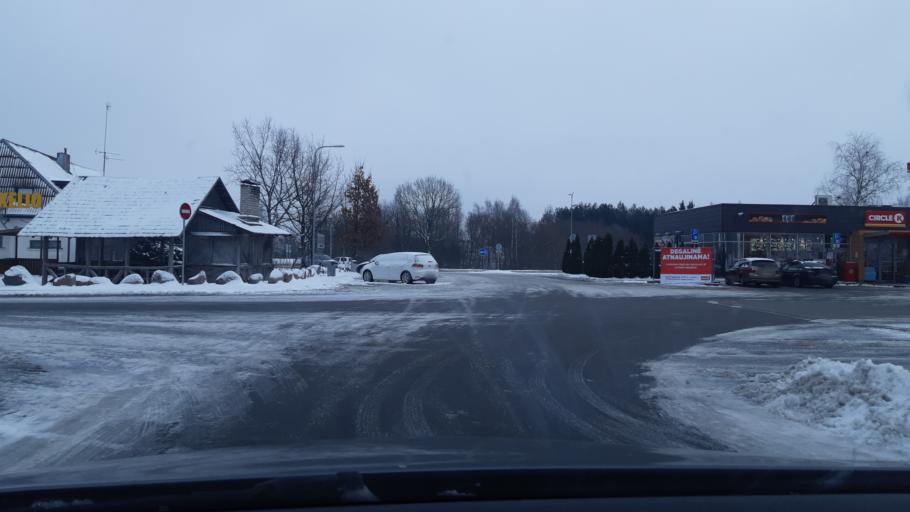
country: LT
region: Kauno apskritis
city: Dainava (Kaunas)
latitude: 54.9339
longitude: 23.9650
